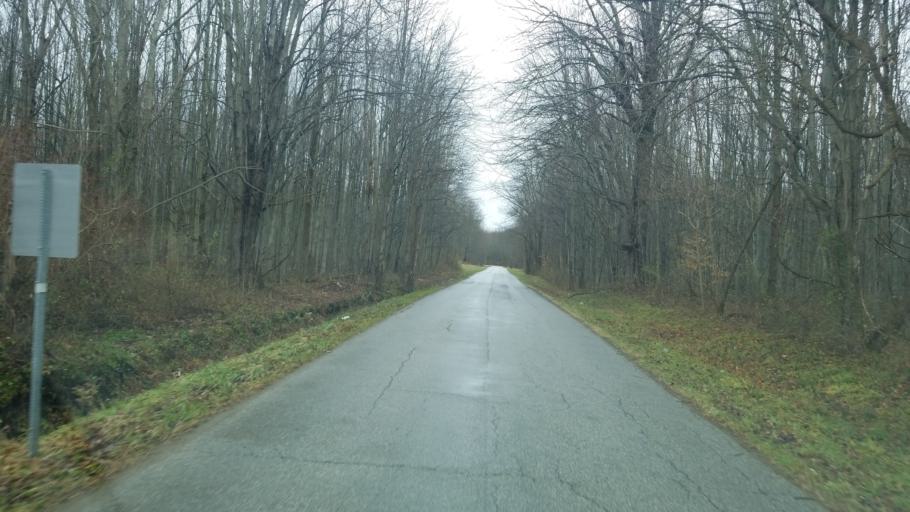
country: US
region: Ohio
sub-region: Ashtabula County
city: North Kingsville
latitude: 41.9091
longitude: -80.7070
